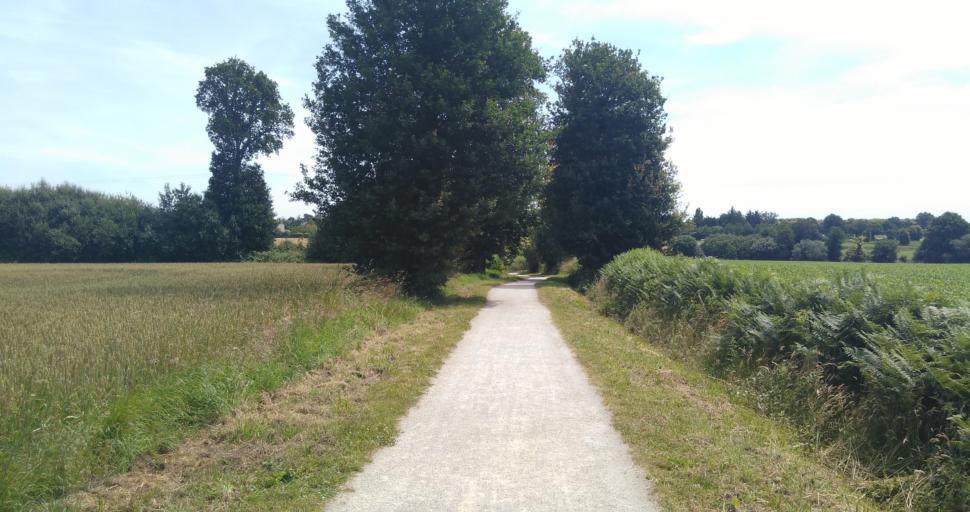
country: FR
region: Brittany
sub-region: Departement d'Ille-et-Vilaine
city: La Meziere
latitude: 48.2190
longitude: -1.7669
